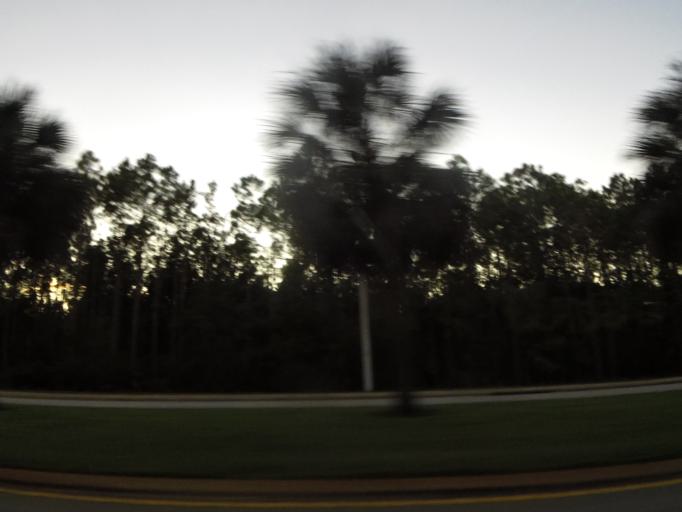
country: US
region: Florida
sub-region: Flagler County
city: Palm Coast
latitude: 29.5964
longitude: -81.2662
